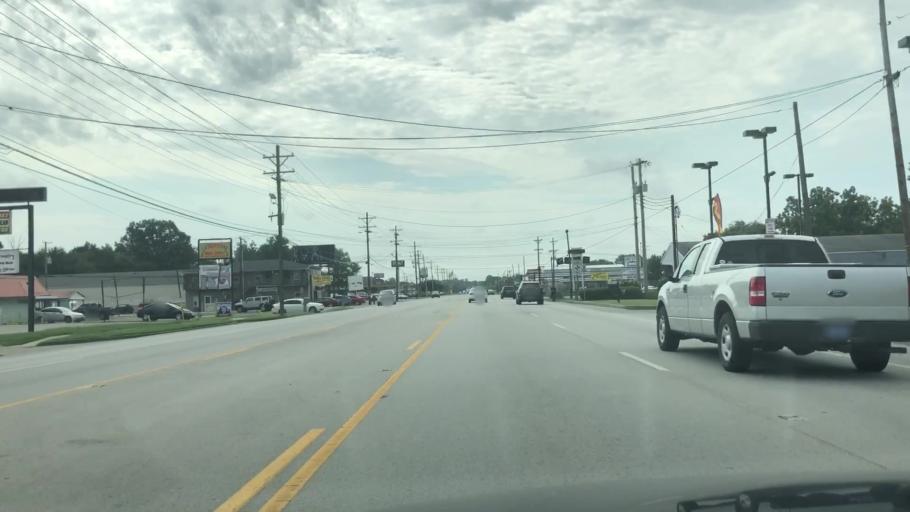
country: US
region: Kentucky
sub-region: Jefferson County
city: Audubon Park
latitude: 38.1728
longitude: -85.7108
